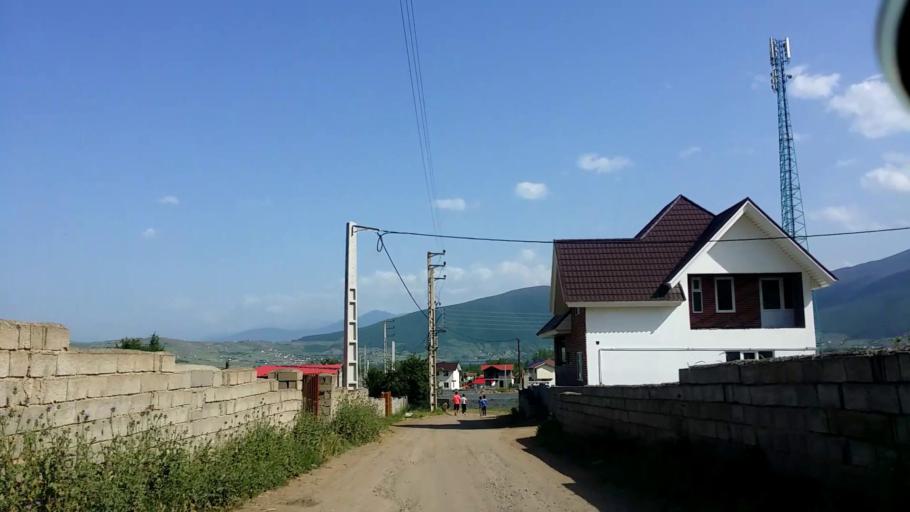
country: IR
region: Mazandaran
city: `Abbasabad
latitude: 36.5460
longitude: 51.1866
